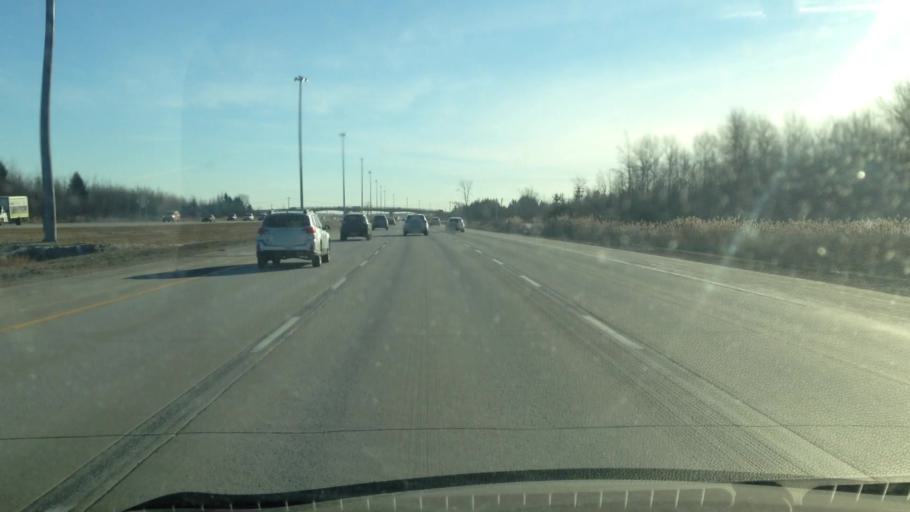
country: CA
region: Quebec
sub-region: Laurentides
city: Saint-Jerome
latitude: 45.7395
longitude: -73.9943
